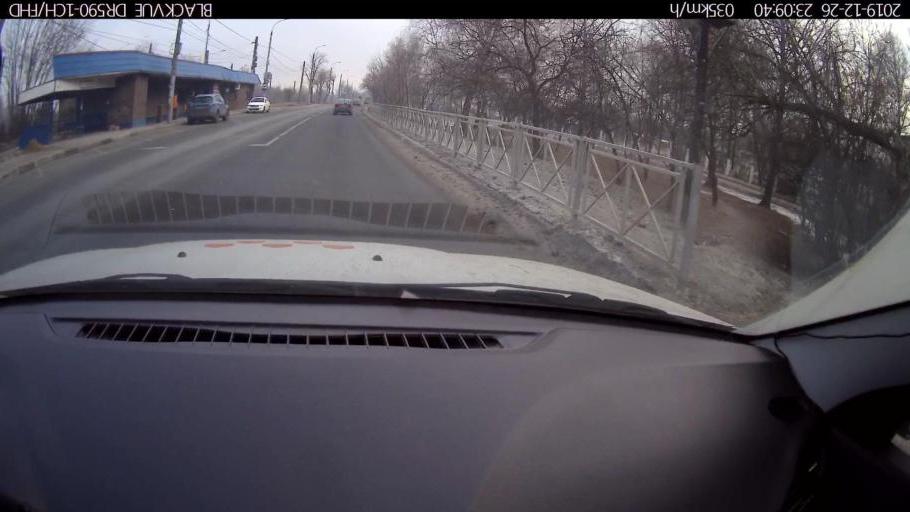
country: RU
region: Nizjnij Novgorod
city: Gorbatovka
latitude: 56.2063
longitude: 43.7701
